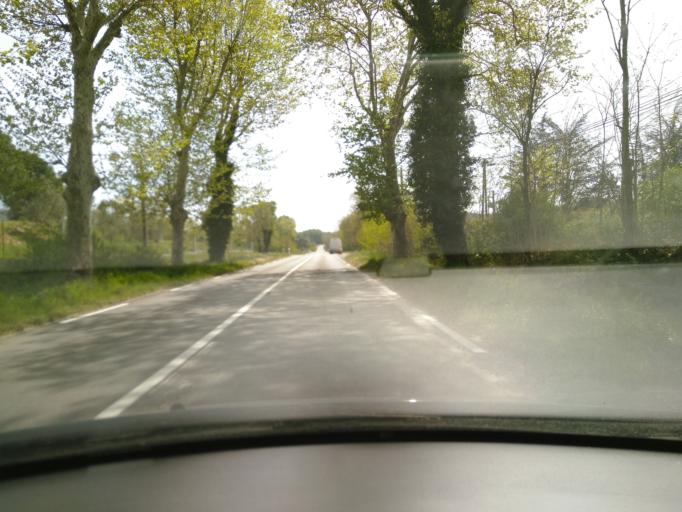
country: FR
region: Rhone-Alpes
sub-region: Departement de la Drome
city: Malataverne
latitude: 44.4949
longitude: 4.7431
